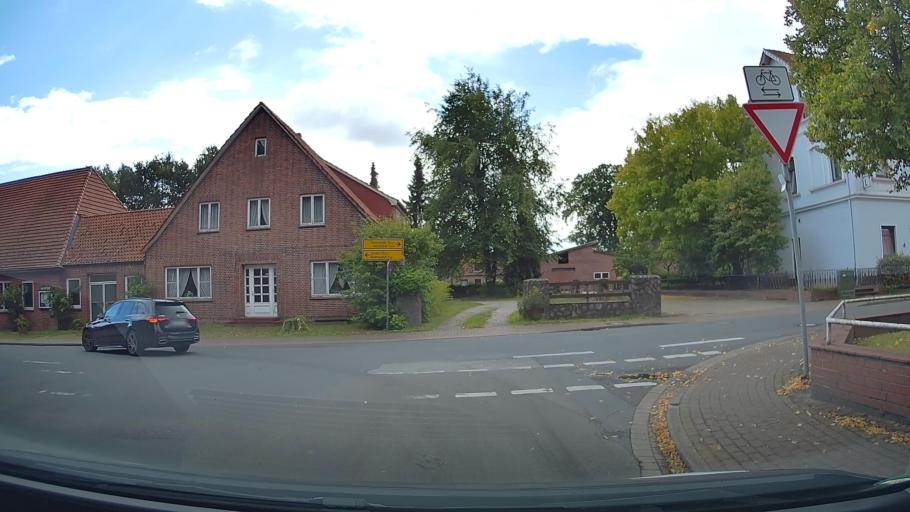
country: DE
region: Lower Saxony
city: Rhade
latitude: 53.3285
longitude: 9.1151
